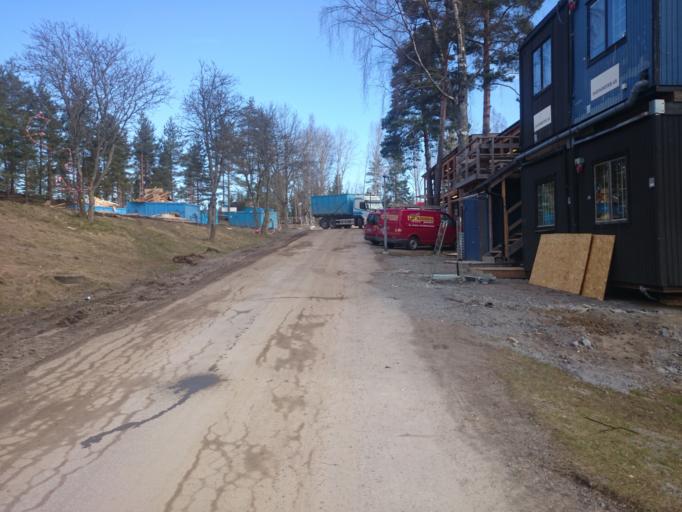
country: SE
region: Stockholm
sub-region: Botkyrka Kommun
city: Tumba
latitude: 59.2022
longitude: 17.8032
